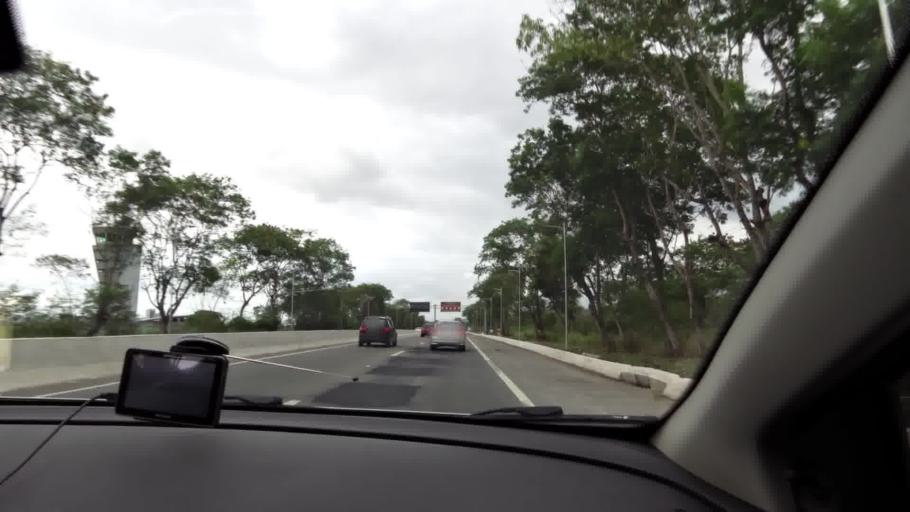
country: BR
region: Espirito Santo
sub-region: Vila Velha
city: Vila Velha
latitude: -20.2509
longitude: -40.2867
